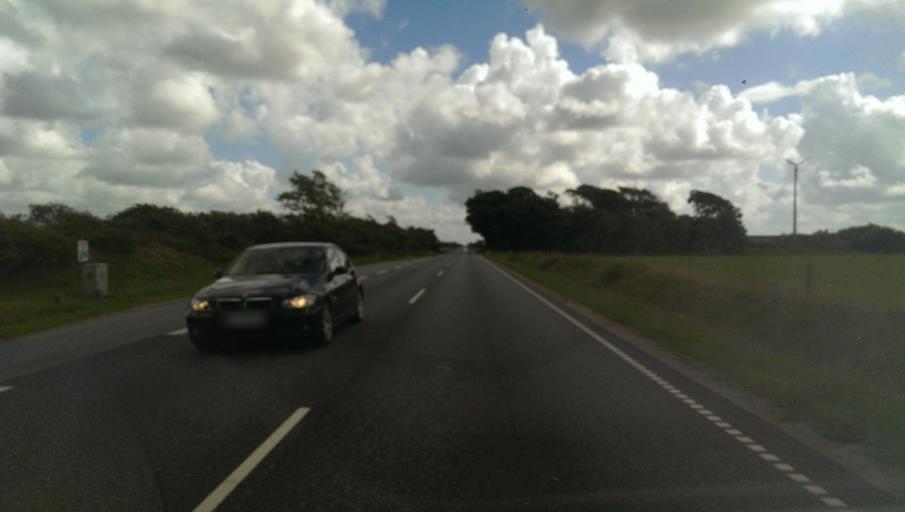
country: DK
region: Central Jutland
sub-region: Ringkobing-Skjern Kommune
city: Ringkobing
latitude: 56.1743
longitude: 8.2877
